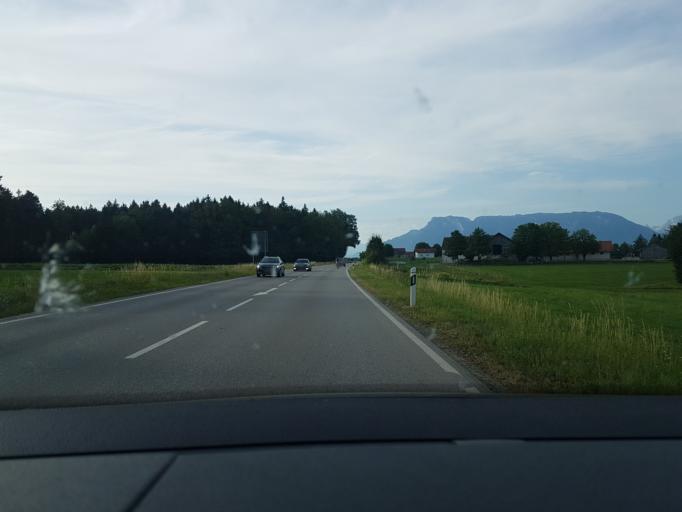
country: DE
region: Bavaria
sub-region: Upper Bavaria
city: Ainring
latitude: 47.8552
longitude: 12.9372
